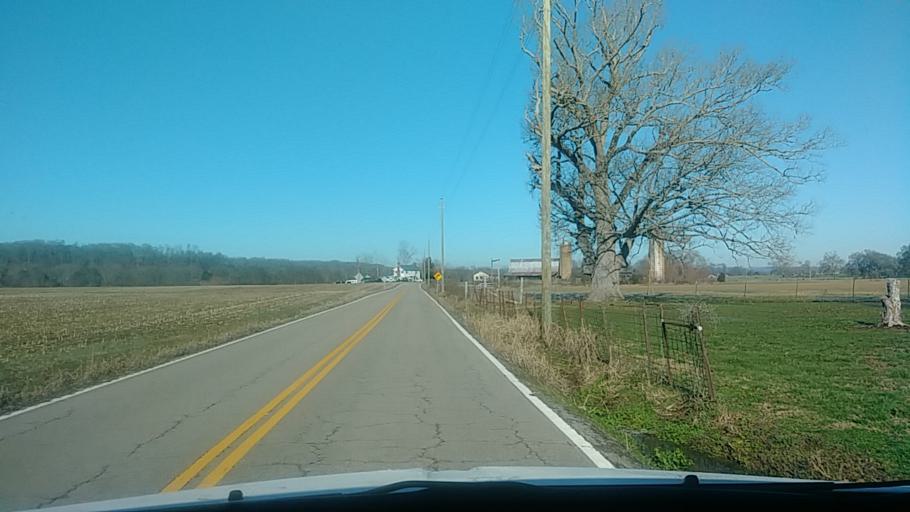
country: US
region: Tennessee
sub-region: Jefferson County
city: White Pine
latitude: 36.1311
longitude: -83.1288
